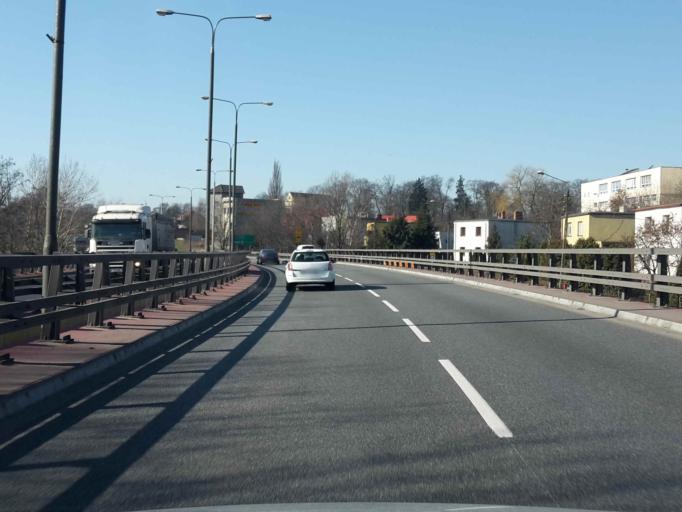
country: PL
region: Greater Poland Voivodeship
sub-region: Powiat gnieznienski
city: Gniezno
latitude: 52.5407
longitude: 17.5920
